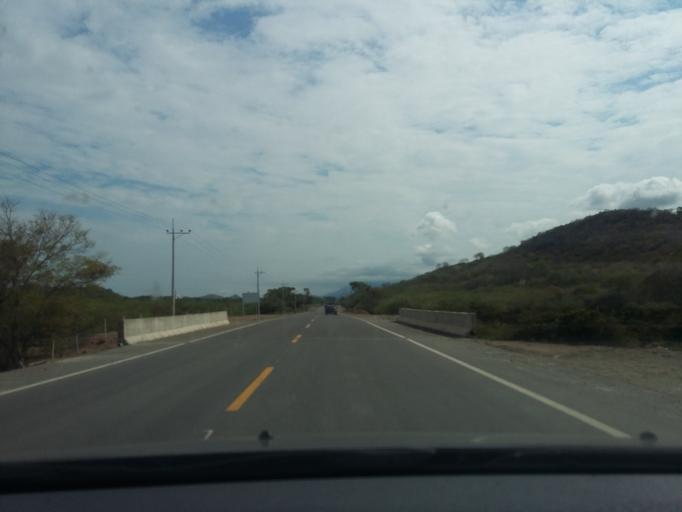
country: CO
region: Tolima
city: Ambalema
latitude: 4.7668
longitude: -74.7668
